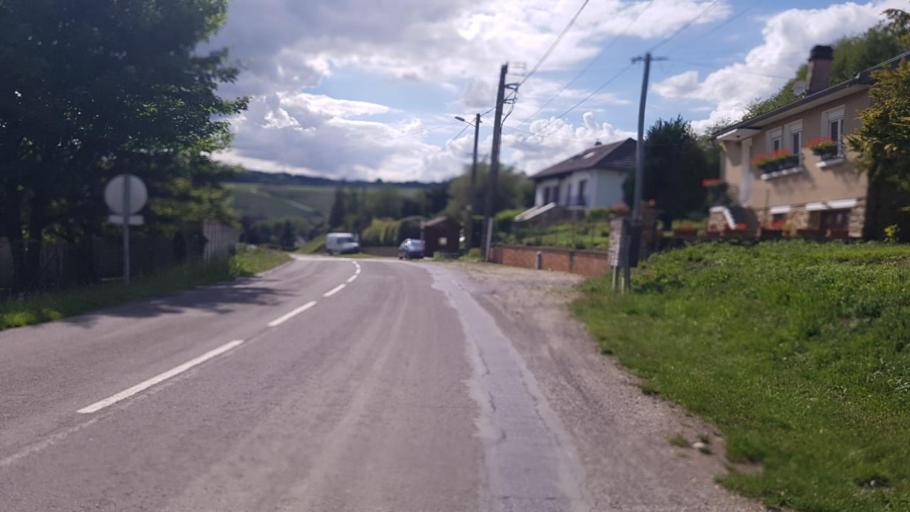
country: FR
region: Picardie
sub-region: Departement de l'Aisne
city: Crezancy
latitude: 49.0884
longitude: 3.5458
